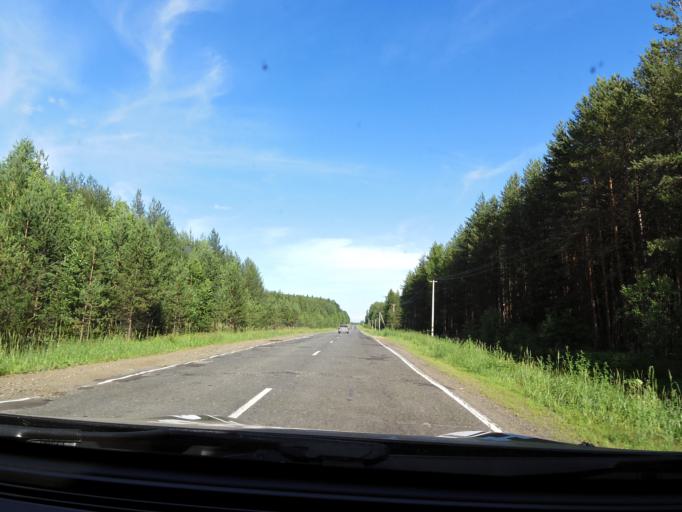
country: RU
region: Kirov
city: Belaya Kholunitsa
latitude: 58.9066
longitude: 51.0154
